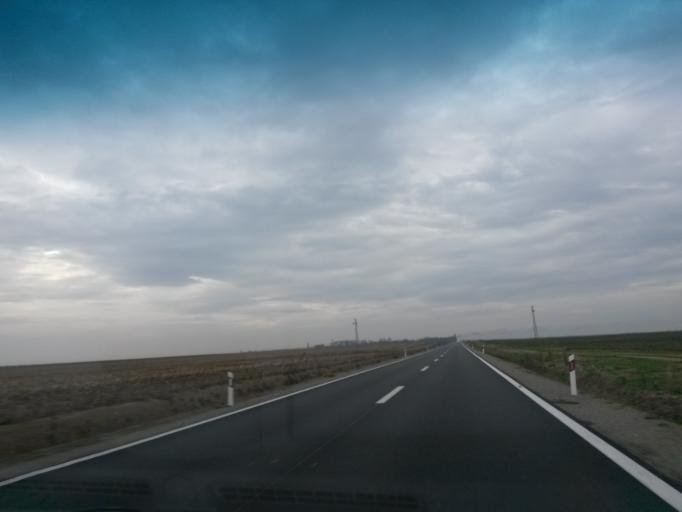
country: HR
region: Osjecko-Baranjska
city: Sarvas
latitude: 45.5083
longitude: 18.7944
